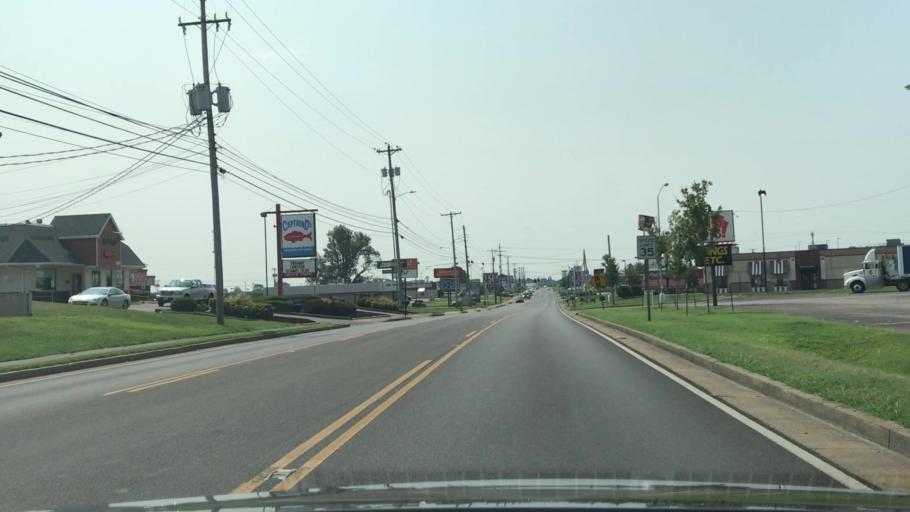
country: US
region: Kentucky
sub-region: Graves County
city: Mayfield
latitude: 36.7245
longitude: -88.6284
